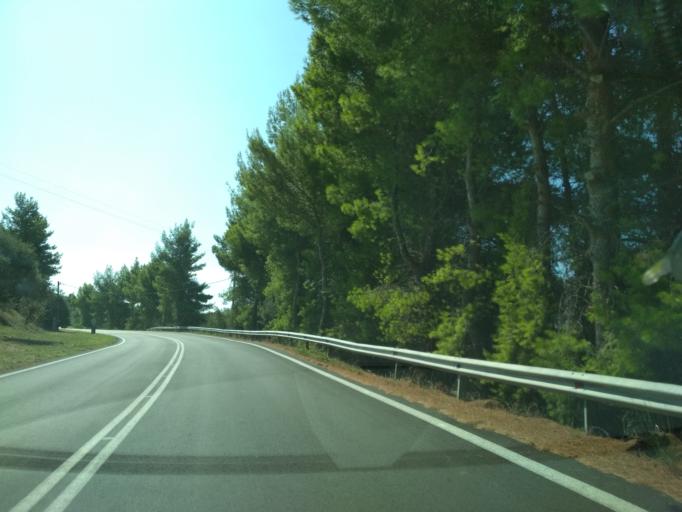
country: GR
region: Central Greece
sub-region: Nomos Evvoias
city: Roviai
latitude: 38.8229
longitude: 23.2281
